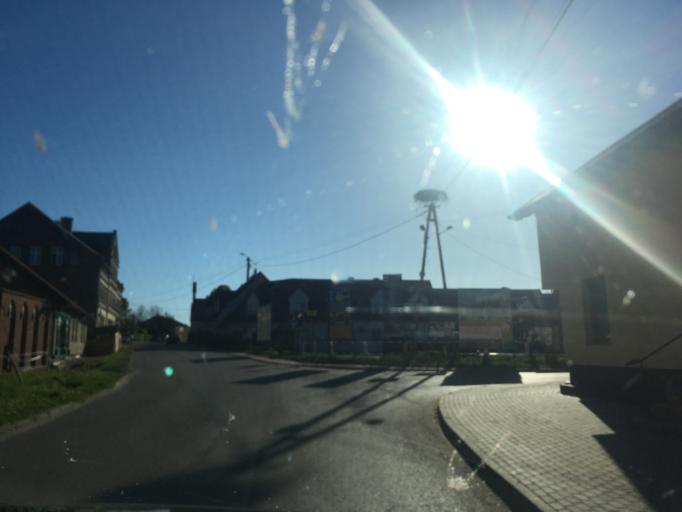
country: PL
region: Warmian-Masurian Voivodeship
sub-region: Powiat piski
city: Ruciane-Nida
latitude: 53.6886
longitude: 21.4968
